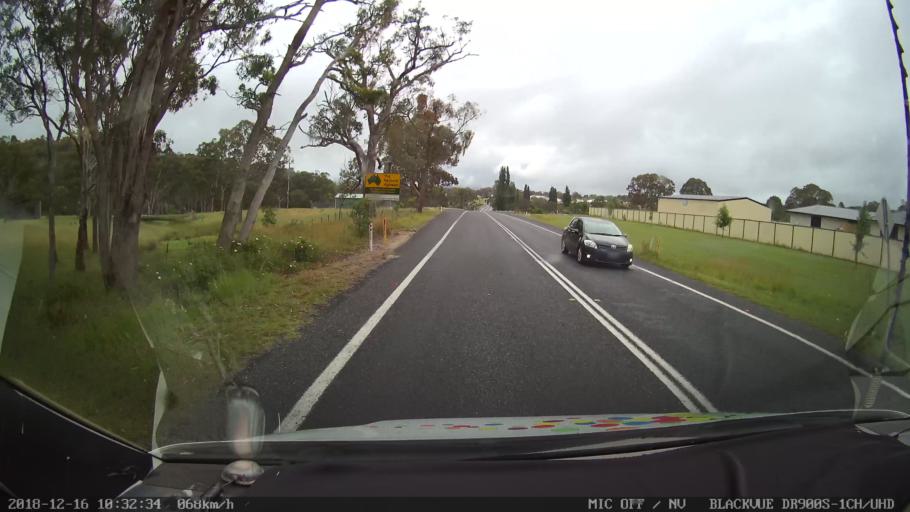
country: AU
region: New South Wales
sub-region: Tenterfield Municipality
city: Carrolls Creek
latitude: -29.0712
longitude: 152.0123
